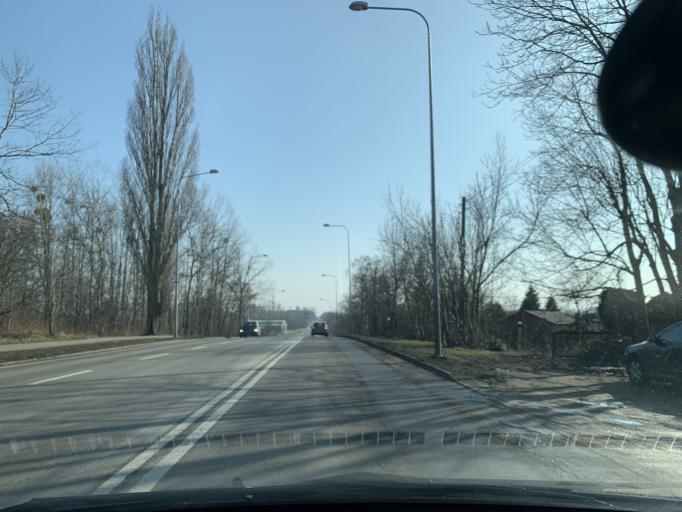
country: PL
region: Silesian Voivodeship
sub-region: Piekary Slaskie
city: Piekary Slaskie
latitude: 50.3644
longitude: 18.9005
